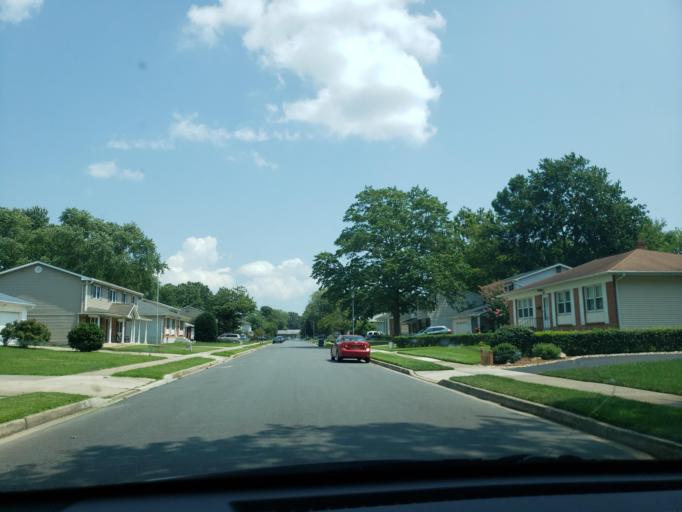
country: US
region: Delaware
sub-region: Kent County
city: Rodney Village
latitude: 39.1350
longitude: -75.5374
